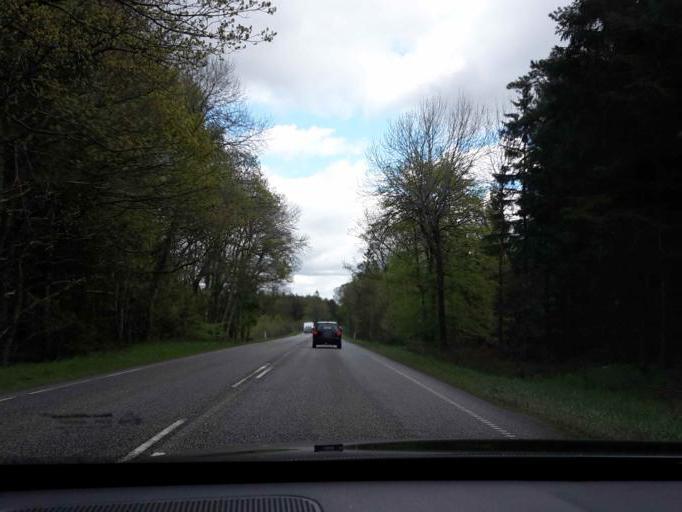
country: DK
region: Central Jutland
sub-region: Norddjurs Kommune
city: Auning
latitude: 56.4265
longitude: 10.4464
